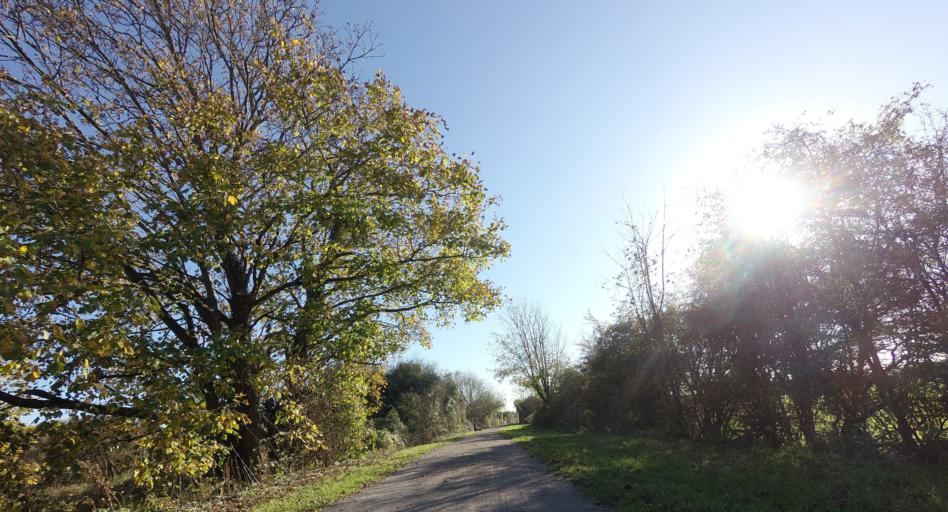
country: GB
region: England
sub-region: West Sussex
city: Shoreham-by-Sea
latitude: 50.8481
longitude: -0.2876
